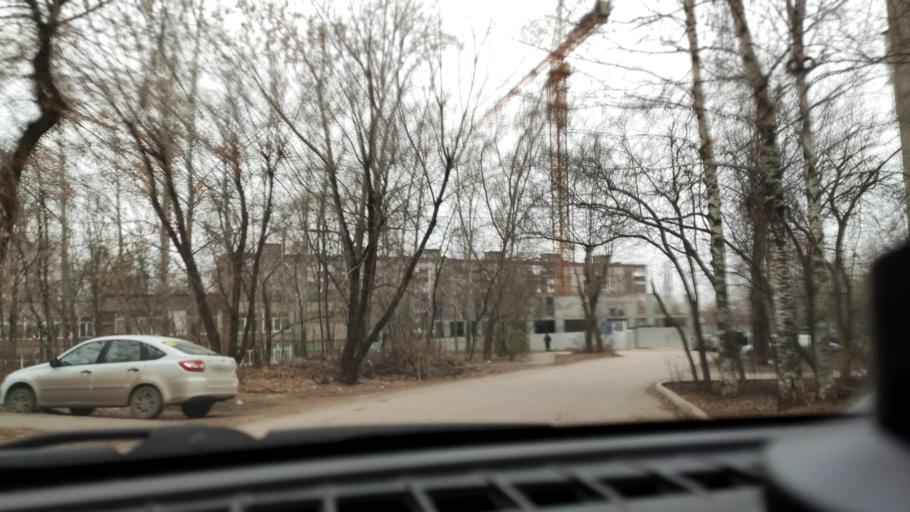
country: RU
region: Perm
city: Perm
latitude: 57.9717
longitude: 56.2249
